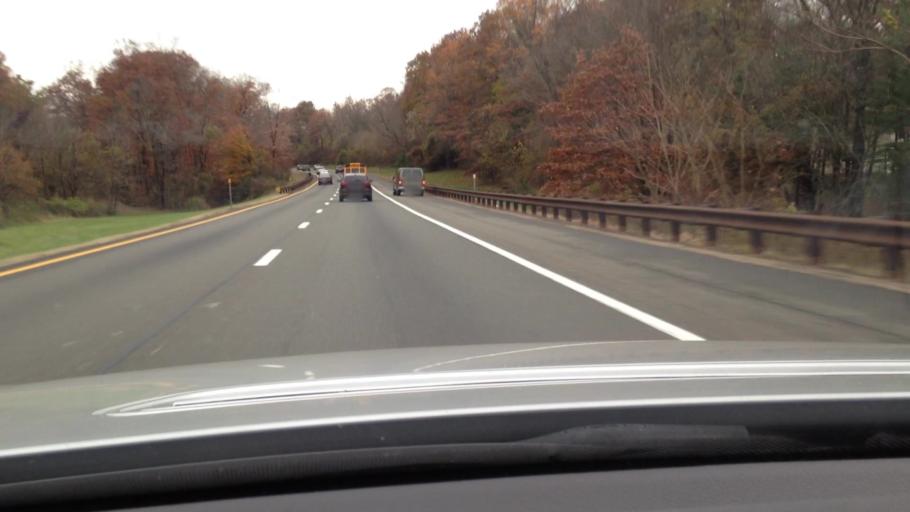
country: US
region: New Jersey
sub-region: Bergen County
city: Woodcliff Lake
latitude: 41.0266
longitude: -74.0694
